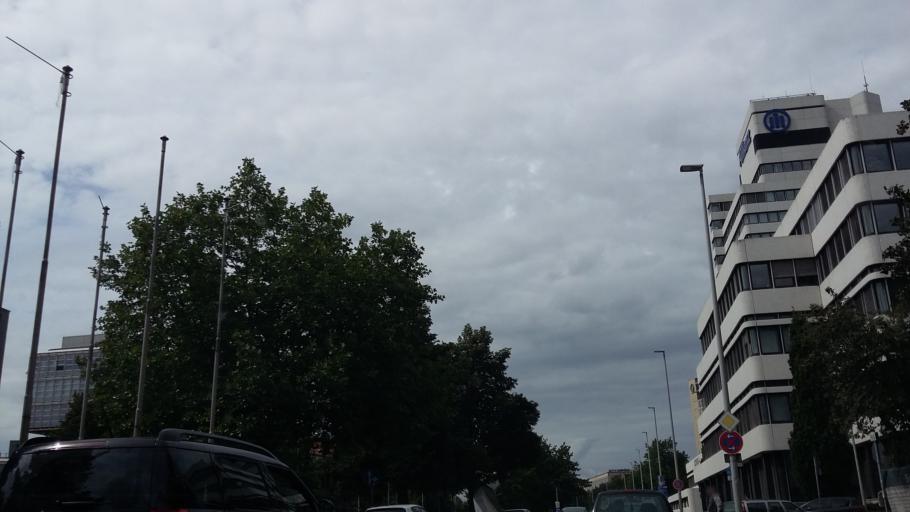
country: DE
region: Lower Saxony
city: Hannover
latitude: 52.3755
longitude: 9.7271
